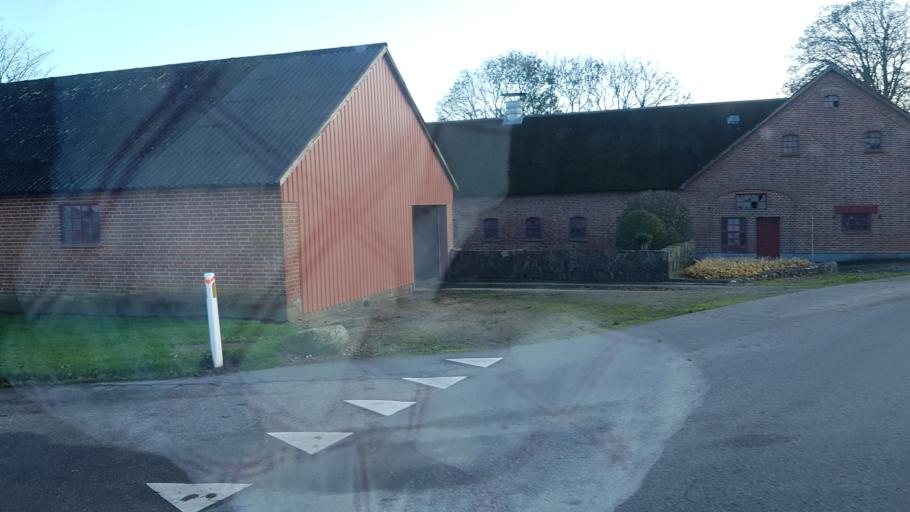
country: DK
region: South Denmark
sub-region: Vejen Kommune
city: Holsted
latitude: 55.4522
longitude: 8.9420
